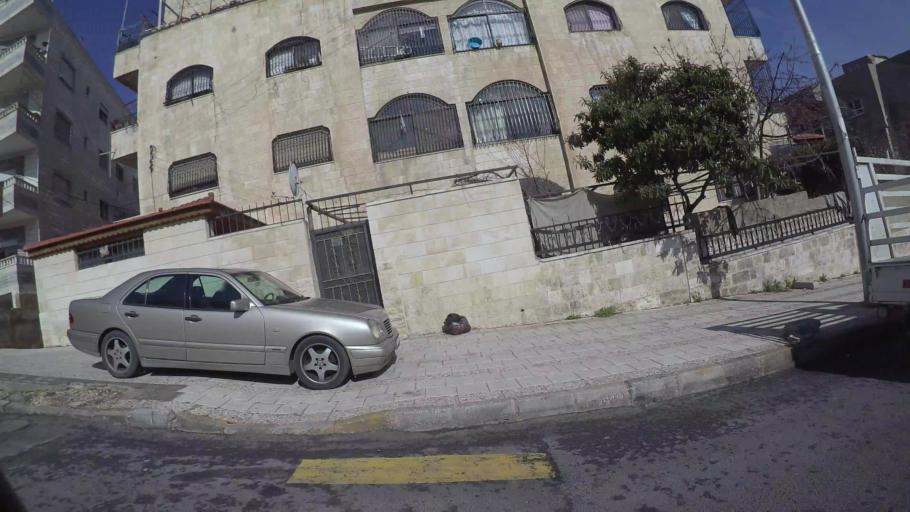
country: JO
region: Amman
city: Al Bunayyat ash Shamaliyah
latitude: 31.9315
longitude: 35.9062
